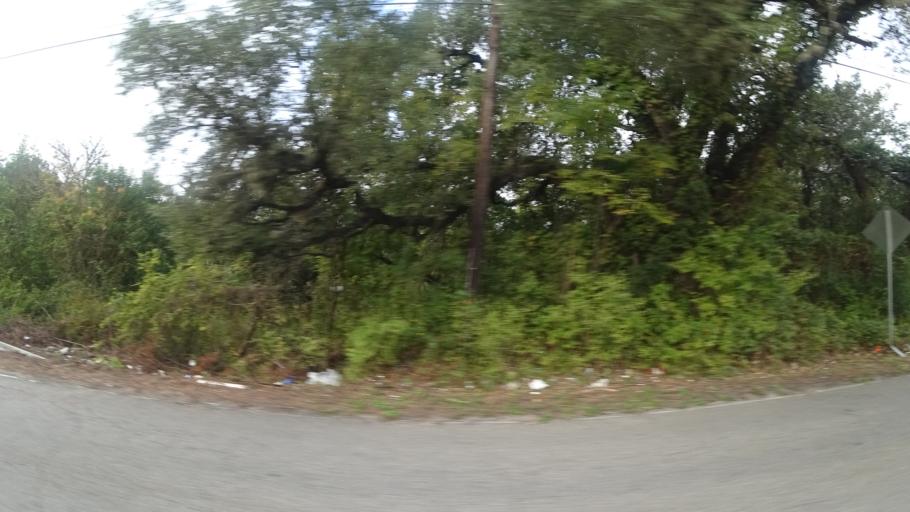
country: US
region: Texas
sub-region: Travis County
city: Pflugerville
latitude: 30.3678
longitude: -97.6551
